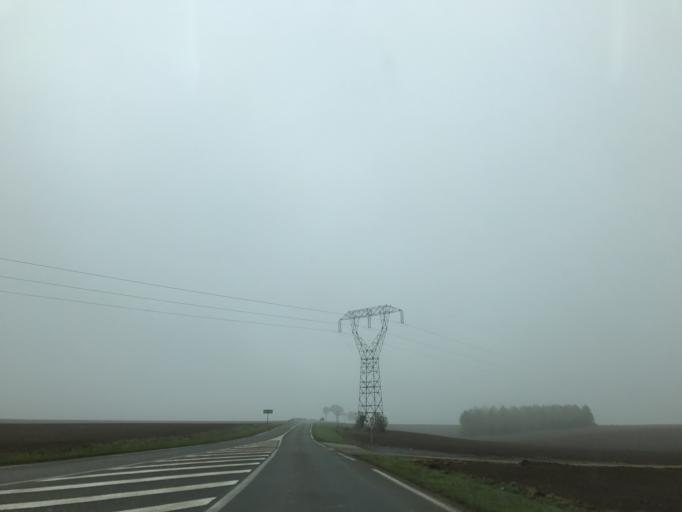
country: FR
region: Nord-Pas-de-Calais
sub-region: Departement du Pas-de-Calais
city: Bapaume
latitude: 50.0501
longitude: 2.9050
